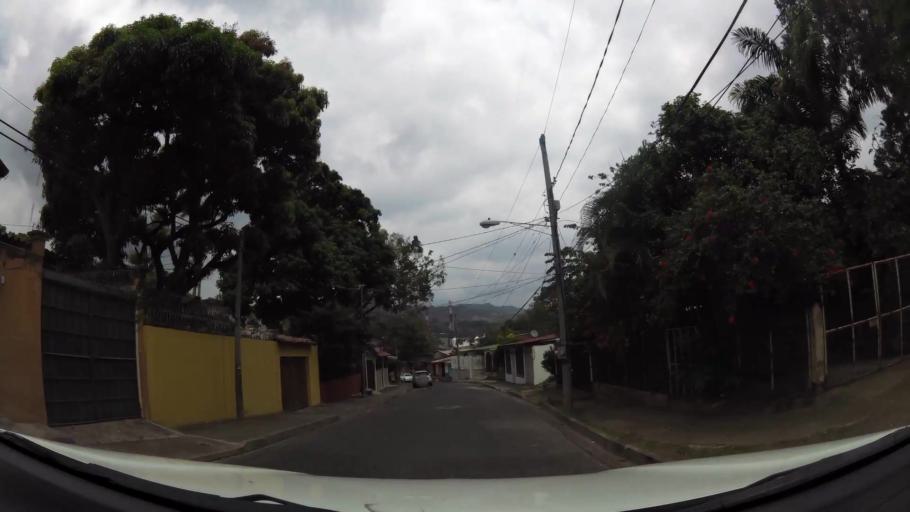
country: NI
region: Matagalpa
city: Matagalpa
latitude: 12.9262
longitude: -85.9149
